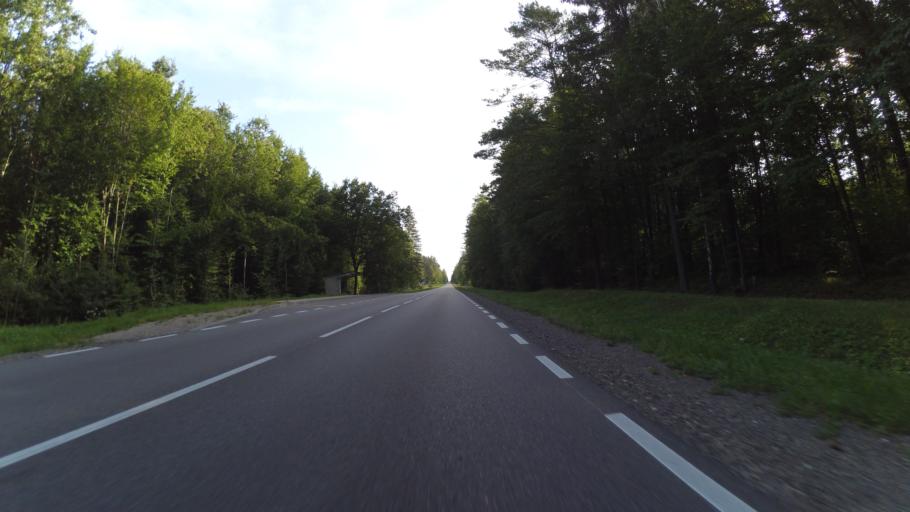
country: PL
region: Podlasie
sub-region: Powiat bialostocki
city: Czarna Bialostocka
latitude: 53.2699
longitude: 23.2655
